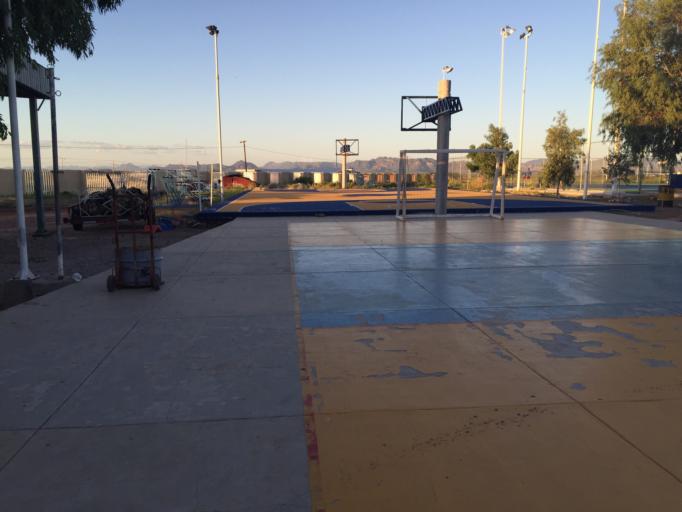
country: MX
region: Sonora
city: Heroica Guaymas
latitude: 27.9691
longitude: -110.9195
